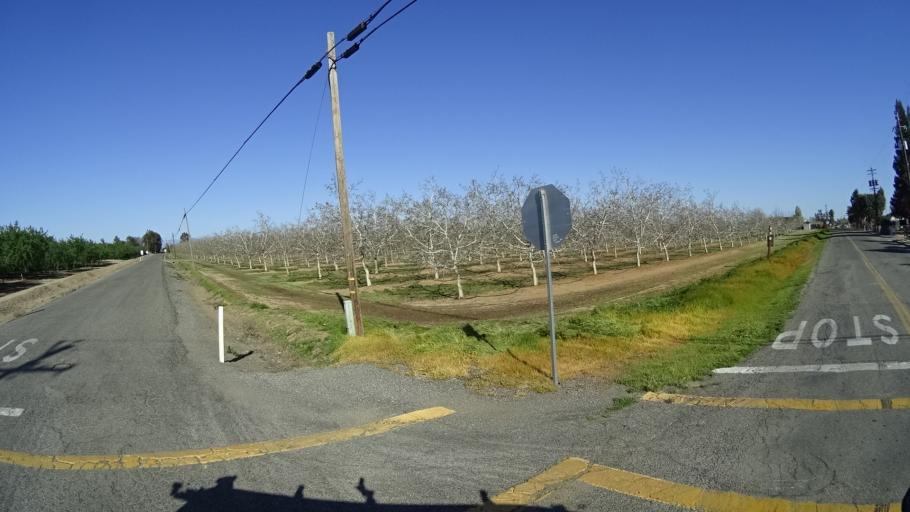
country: US
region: California
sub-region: Glenn County
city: Hamilton City
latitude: 39.7969
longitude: -122.0853
